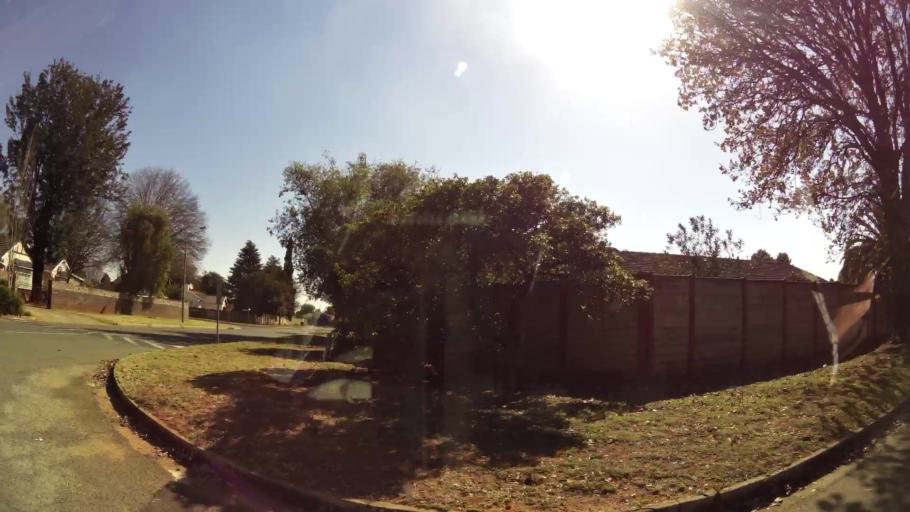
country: ZA
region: Gauteng
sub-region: City of Johannesburg Metropolitan Municipality
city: Modderfontein
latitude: -26.0561
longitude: 28.2056
